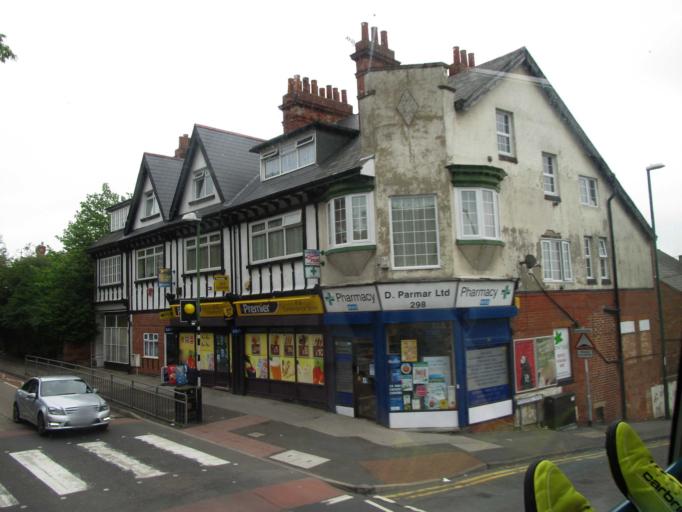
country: GB
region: England
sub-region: Nottingham
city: Nottingham
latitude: 52.9679
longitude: -1.1431
